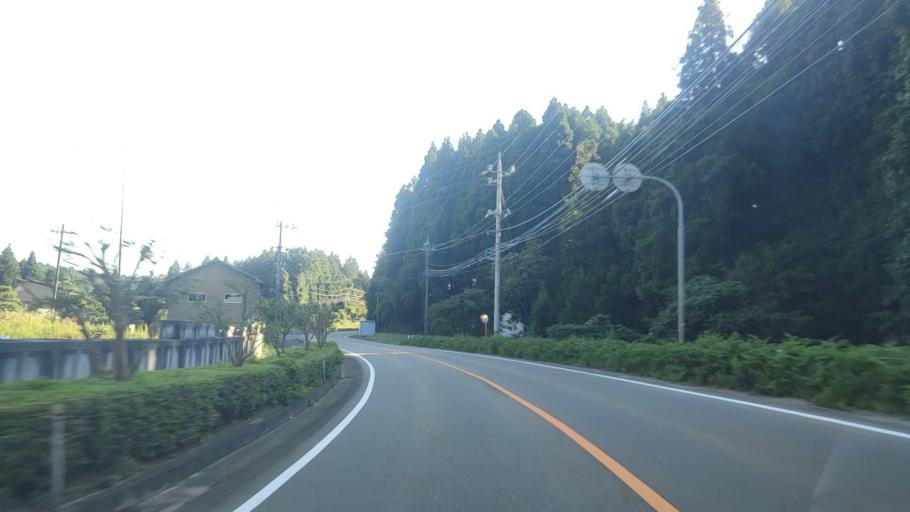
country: JP
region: Ishikawa
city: Nanao
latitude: 37.1199
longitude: 136.8617
